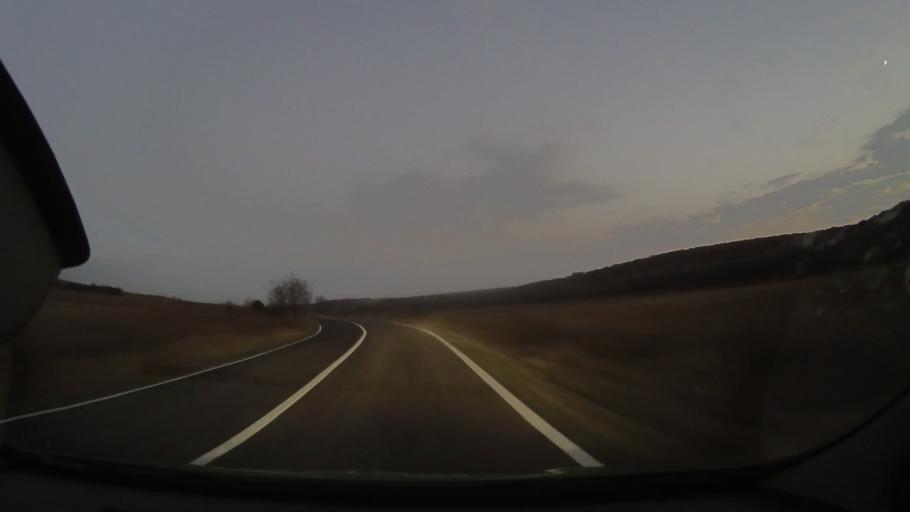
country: RO
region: Constanta
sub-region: Comuna Ion Corvin
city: Ion Corvin
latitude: 44.1060
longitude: 27.7807
